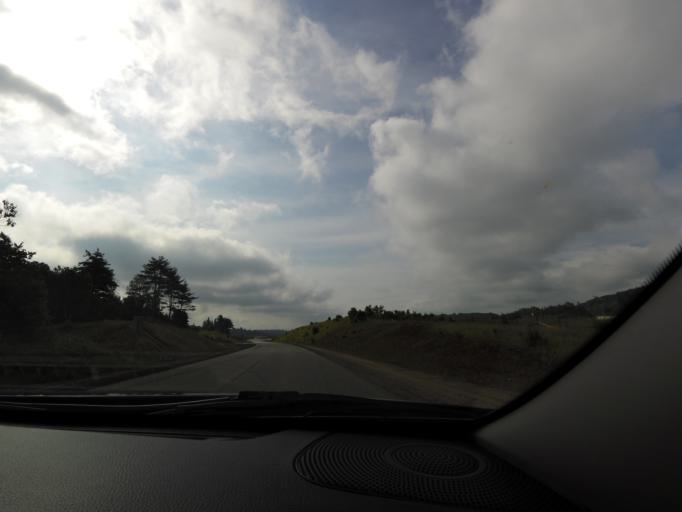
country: CA
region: Ontario
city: Huntsville
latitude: 45.5151
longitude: -79.3086
